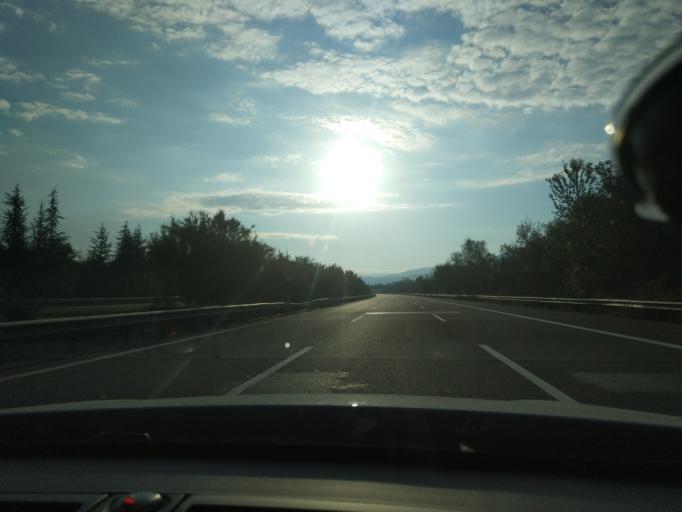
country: TR
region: Duzce
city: Duzce
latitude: 40.7949
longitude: 31.1975
